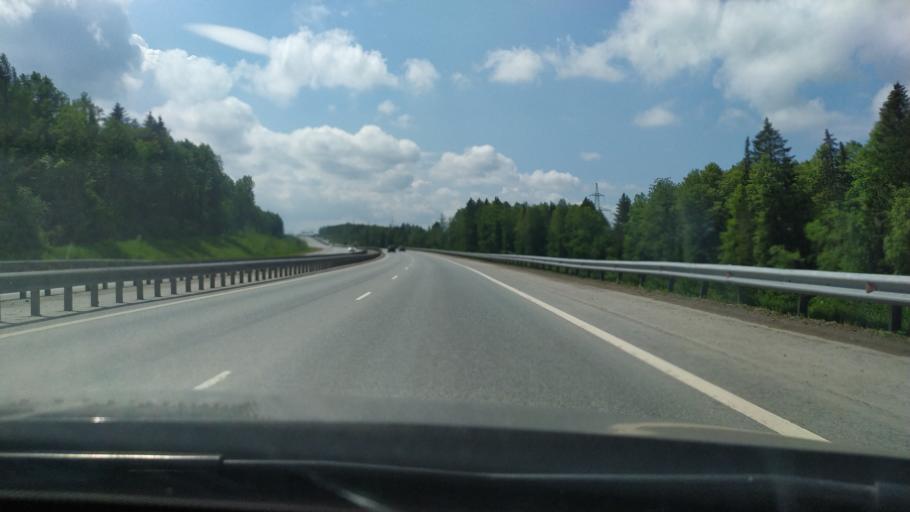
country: RU
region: Perm
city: Ferma
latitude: 58.0132
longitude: 56.4037
